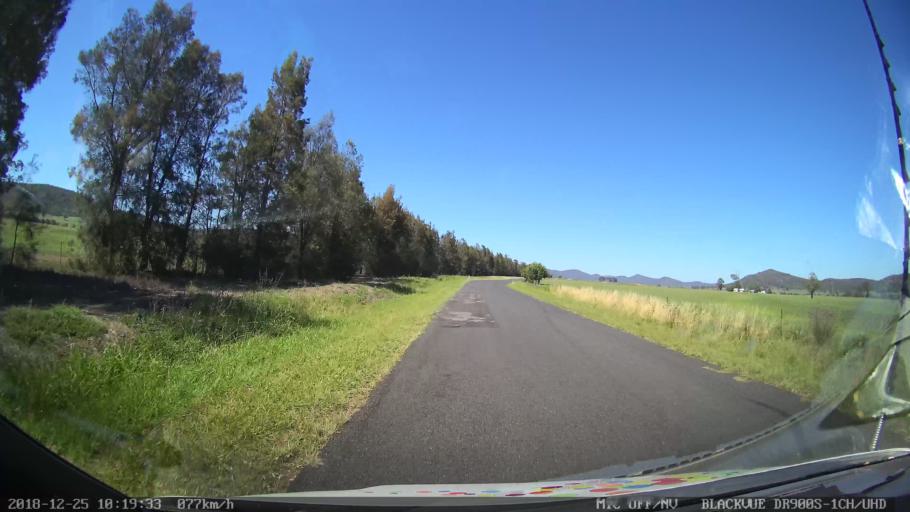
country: AU
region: New South Wales
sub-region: Muswellbrook
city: Denman
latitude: -32.3517
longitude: 150.5576
